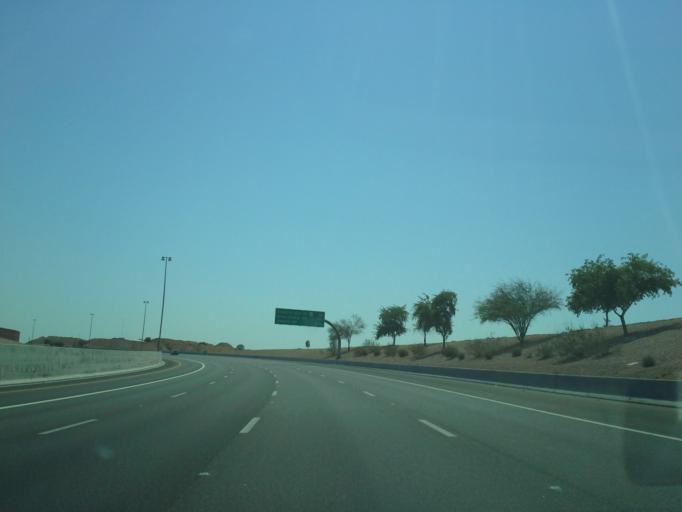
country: US
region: Arizona
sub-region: Maricopa County
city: Mesa
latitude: 33.4655
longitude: -111.8228
